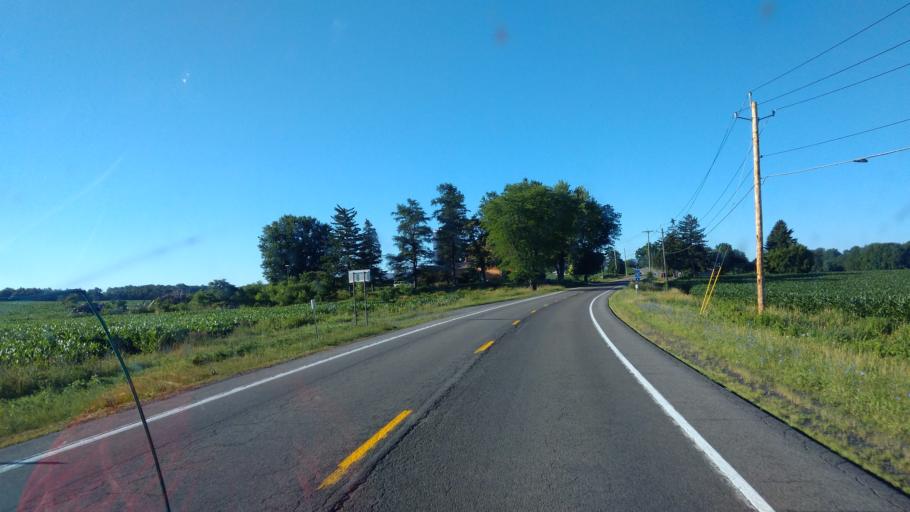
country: US
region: New York
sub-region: Wayne County
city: Lyons
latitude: 43.0354
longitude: -76.9916
